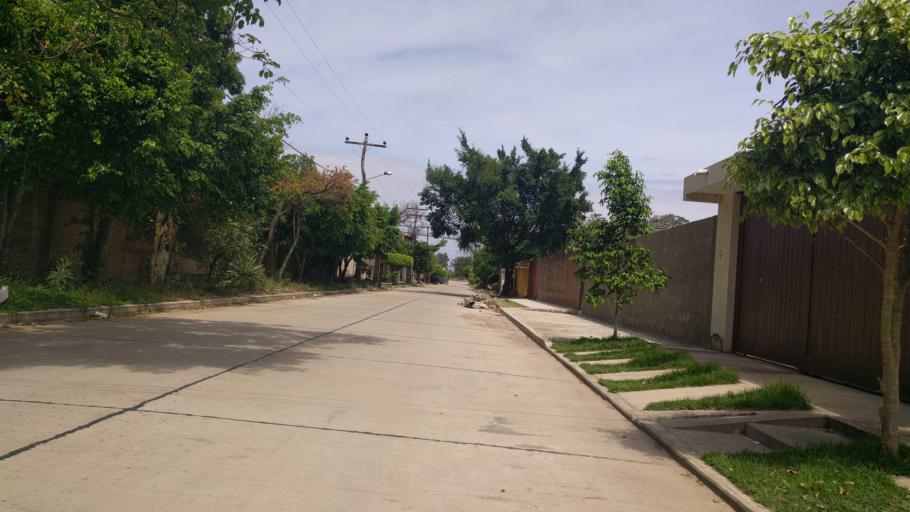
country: BO
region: Santa Cruz
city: Santa Cruz de la Sierra
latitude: -17.8171
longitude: -63.2220
